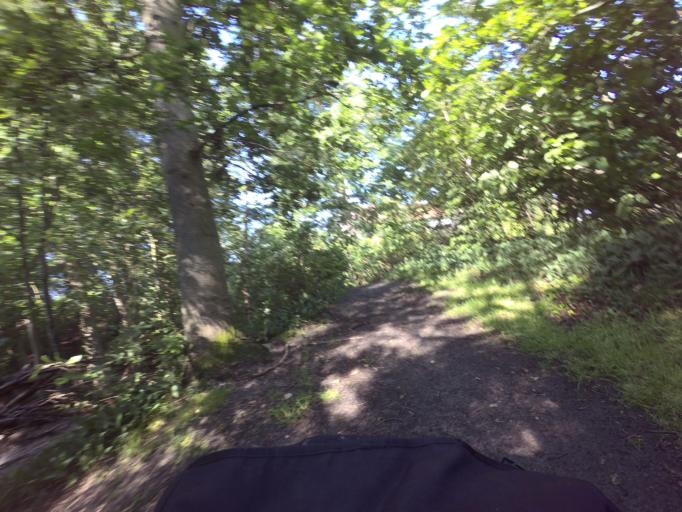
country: SE
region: Skane
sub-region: Hoganas Kommun
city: Hoganas
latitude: 56.1620
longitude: 12.5709
